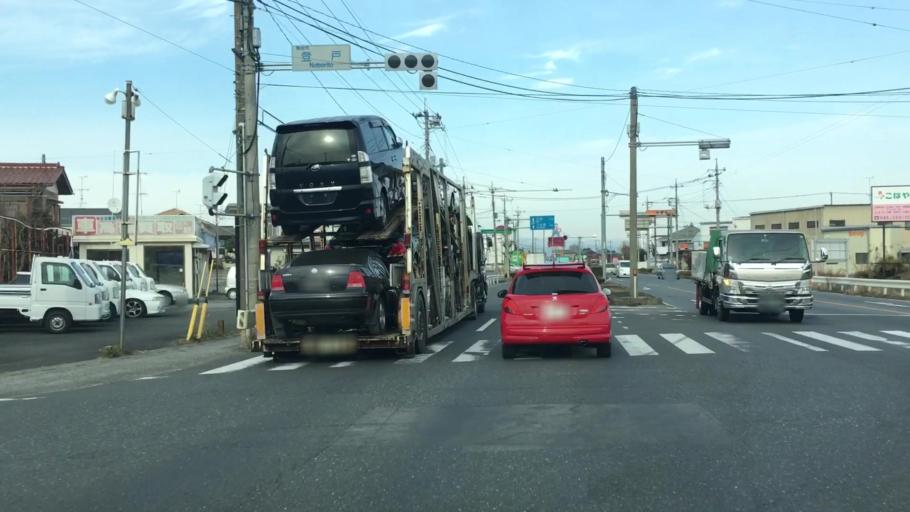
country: JP
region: Saitama
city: Menuma
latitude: 36.2278
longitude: 139.3704
